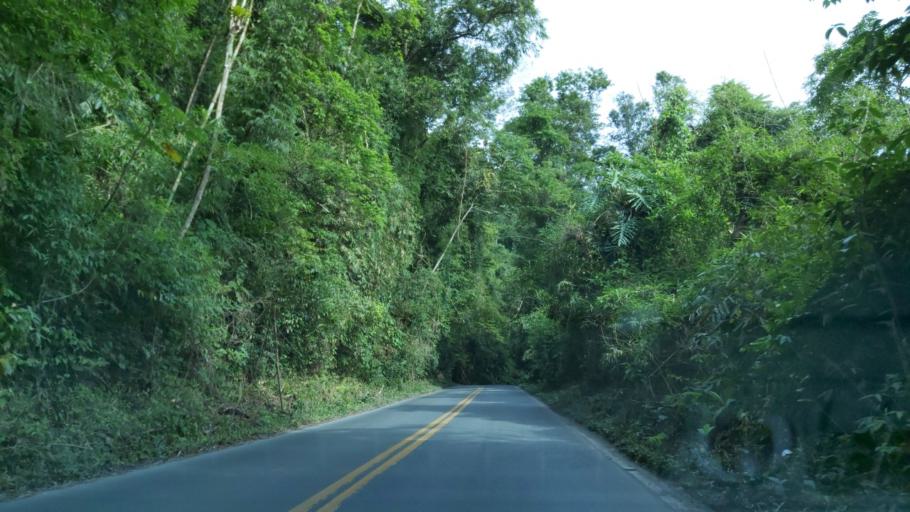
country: BR
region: Sao Paulo
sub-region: Juquia
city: Juquia
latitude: -24.0944
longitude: -47.6158
